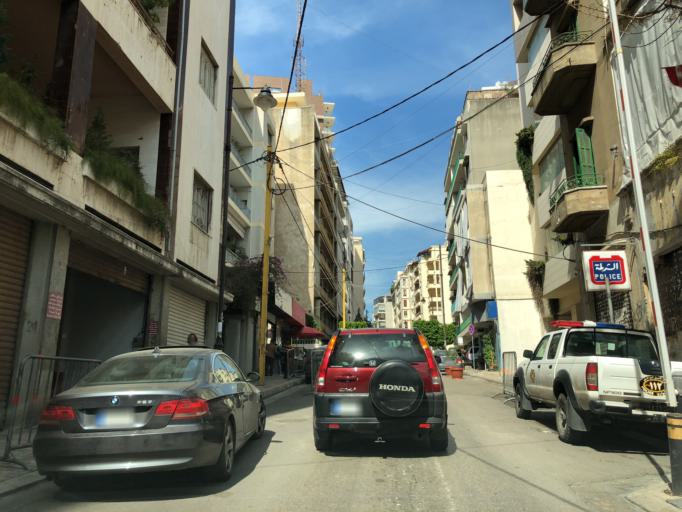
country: LB
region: Beyrouth
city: Beirut
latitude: 33.8850
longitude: 35.5189
